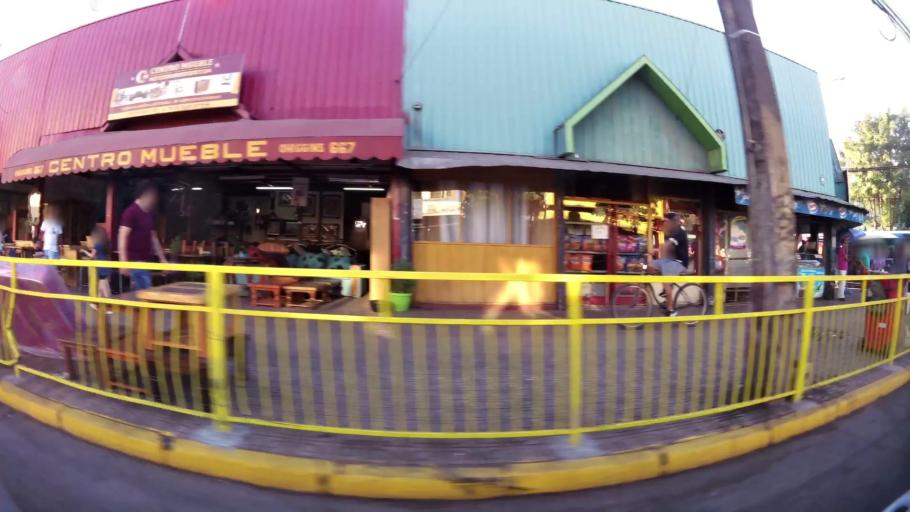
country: CL
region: Maule
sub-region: Provincia de Curico
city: Curico
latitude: -34.9844
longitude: -71.2444
